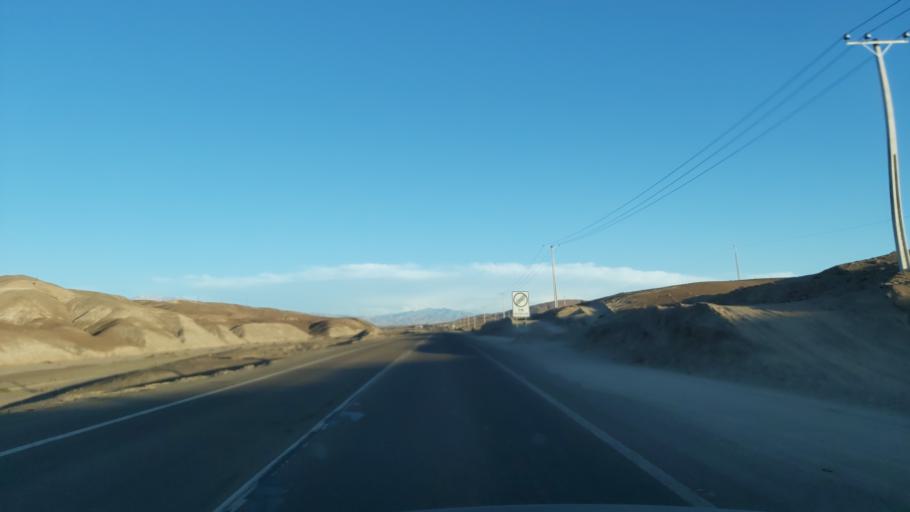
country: CL
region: Atacama
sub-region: Provincia de Chanaral
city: Diego de Almagro
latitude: -26.4202
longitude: -70.0249
